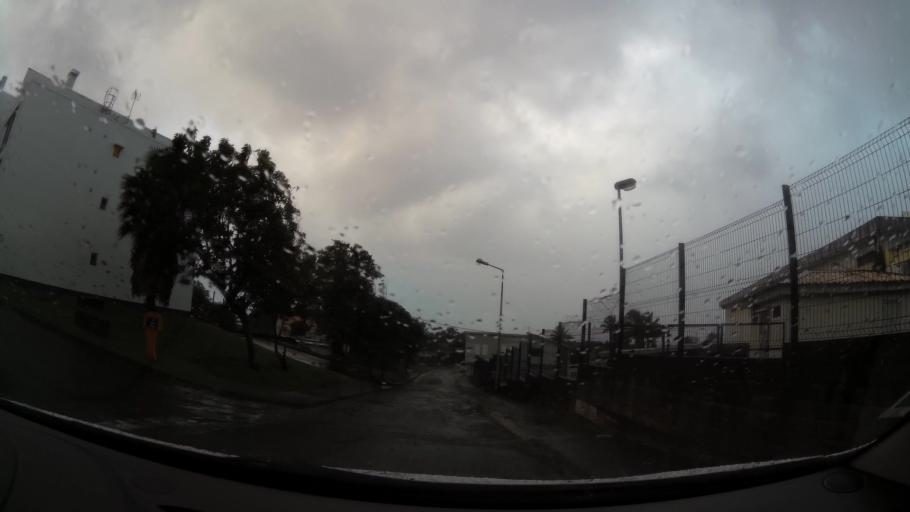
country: RE
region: Reunion
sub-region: Reunion
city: Saint-Benoit
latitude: -21.0438
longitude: 55.7218
